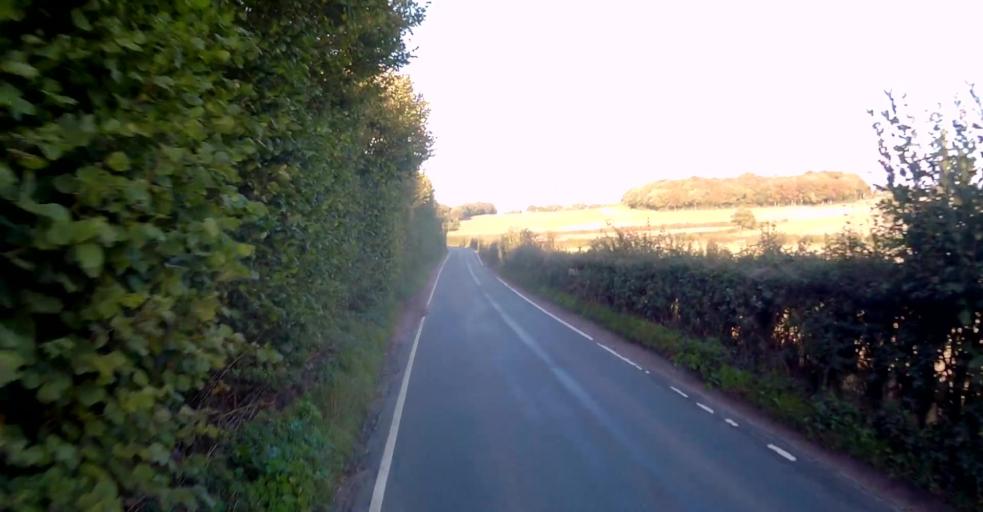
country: GB
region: England
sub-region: Hampshire
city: Long Sutton
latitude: 51.2346
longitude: -0.9260
